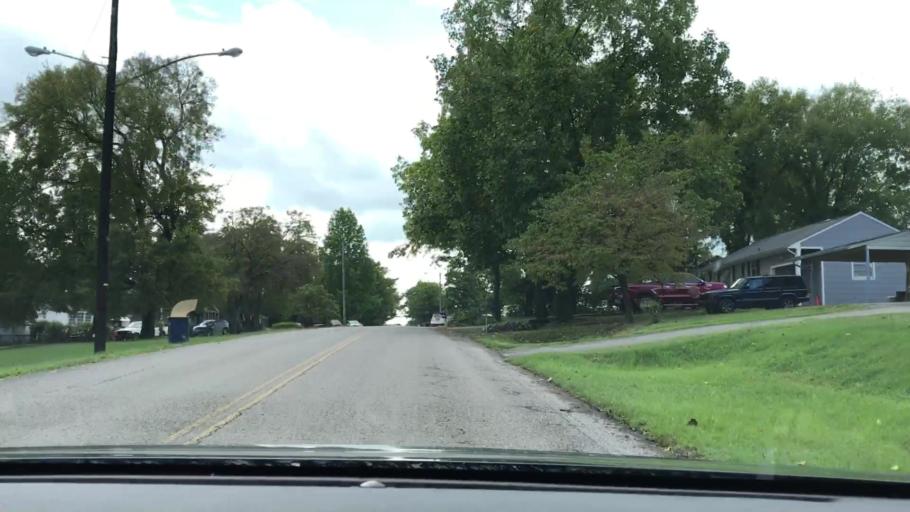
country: US
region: Tennessee
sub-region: Davidson County
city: Oak Hill
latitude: 36.1161
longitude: -86.7653
